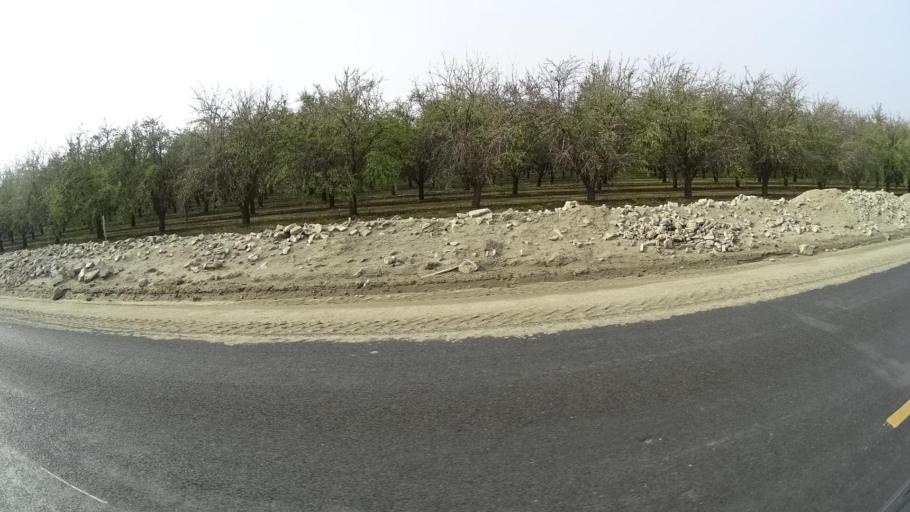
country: US
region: California
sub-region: Kern County
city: Arvin
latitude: 35.1634
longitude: -118.8509
